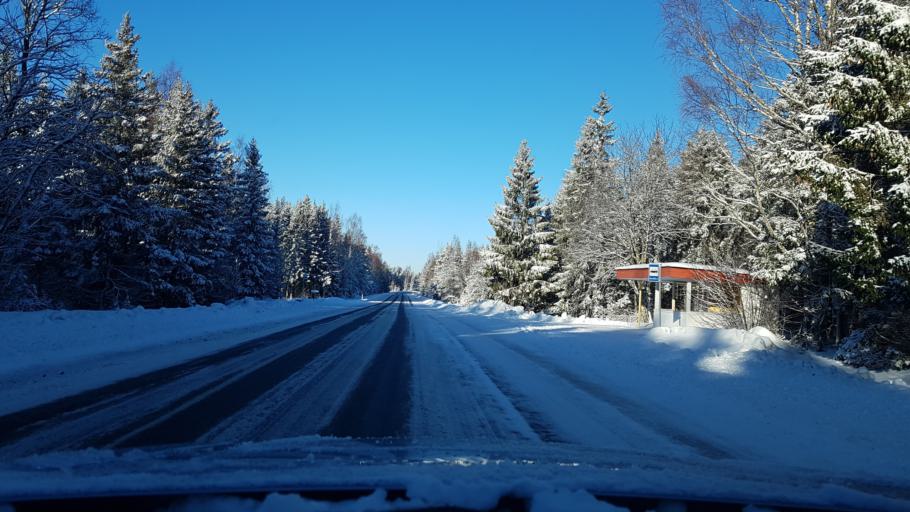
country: EE
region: Hiiumaa
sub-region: Kaerdla linn
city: Kardla
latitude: 58.9758
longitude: 22.8176
